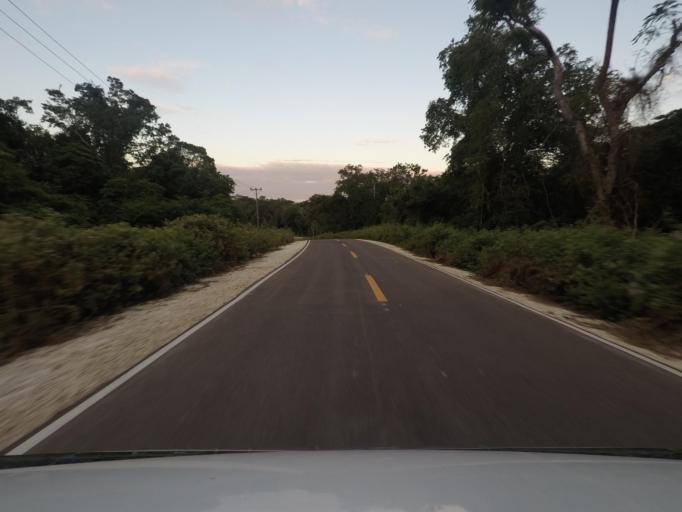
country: TL
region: Lautem
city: Lospalos
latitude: -8.4138
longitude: 127.2966
